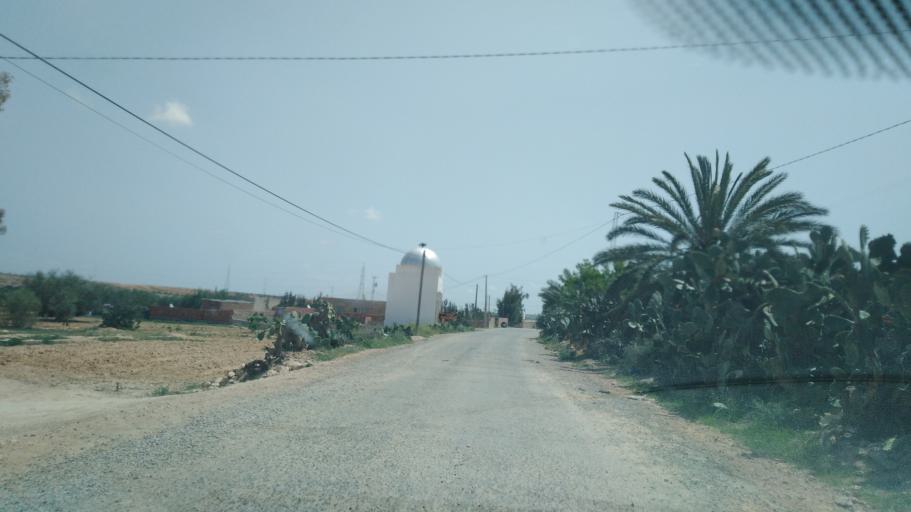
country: TN
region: Safaqis
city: Sfax
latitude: 34.7495
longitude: 10.5689
